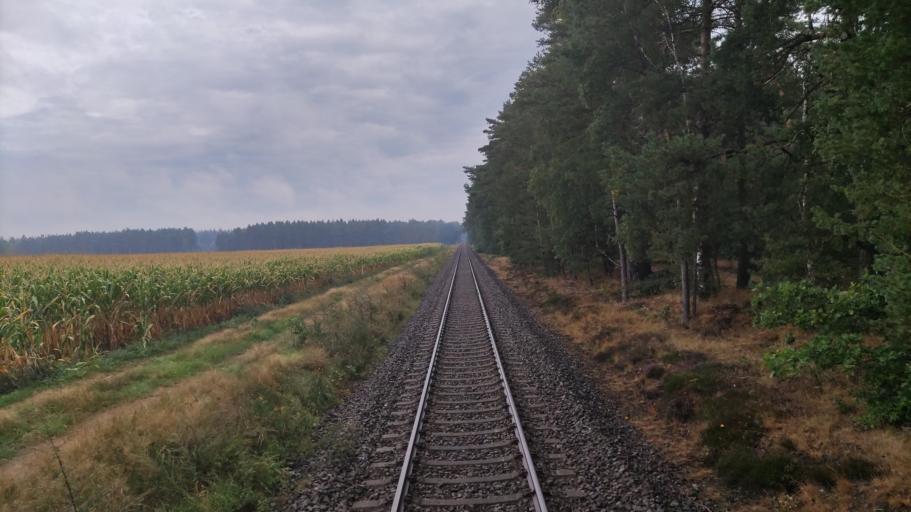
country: DE
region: Lower Saxony
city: Bispingen
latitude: 53.0422
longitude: 9.9400
